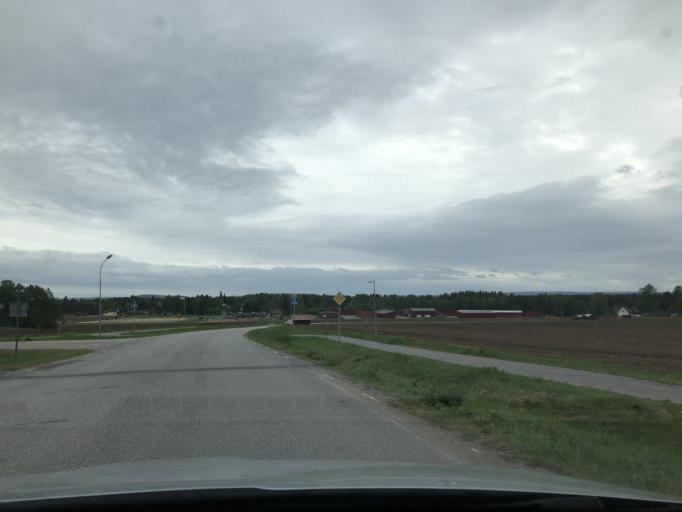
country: SE
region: Norrbotten
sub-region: Pitea Kommun
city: Bergsviken
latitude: 65.3833
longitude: 21.3139
